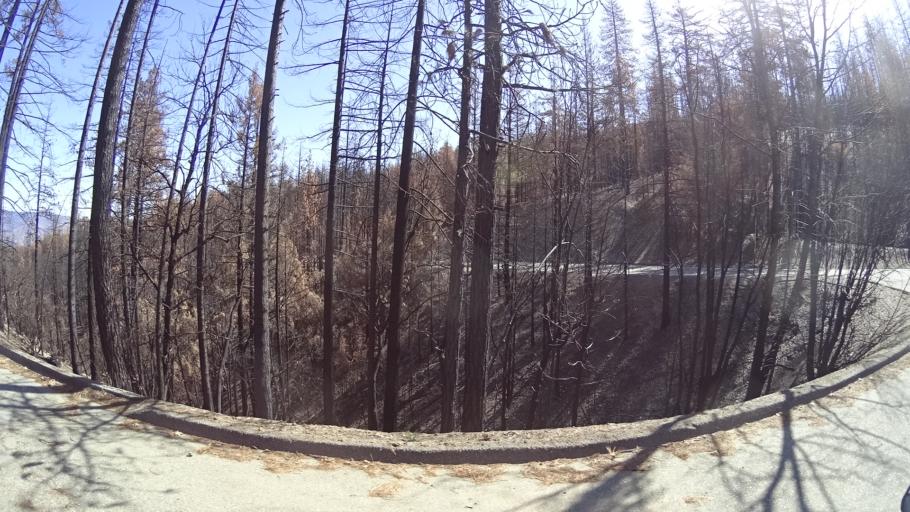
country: US
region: California
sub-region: Tehama County
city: Rancho Tehama Reserve
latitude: 39.6647
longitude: -122.7173
